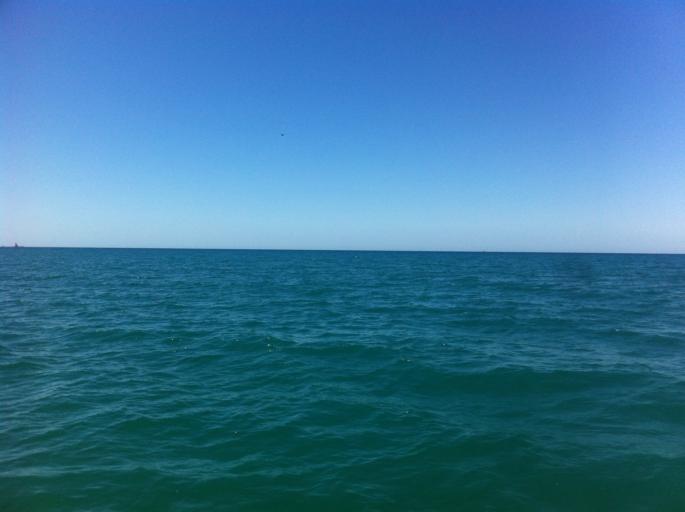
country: MX
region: Sonora
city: Heroica Guaymas
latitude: 27.9629
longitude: -111.0066
